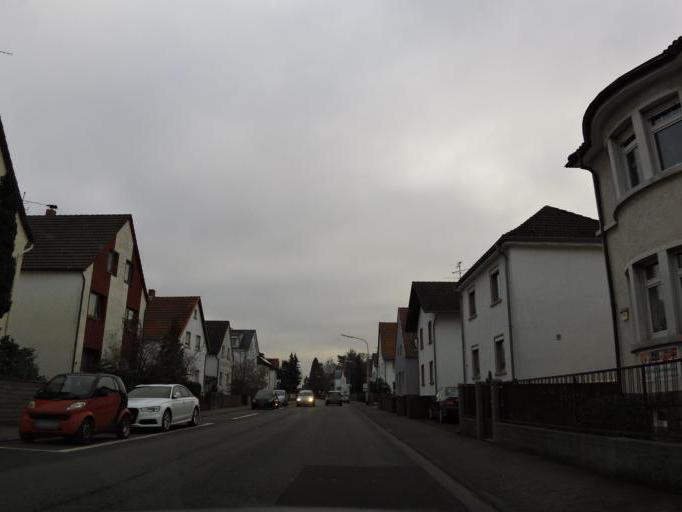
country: DE
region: Hesse
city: Morfelden-Walldorf
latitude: 49.9729
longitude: 8.5548
